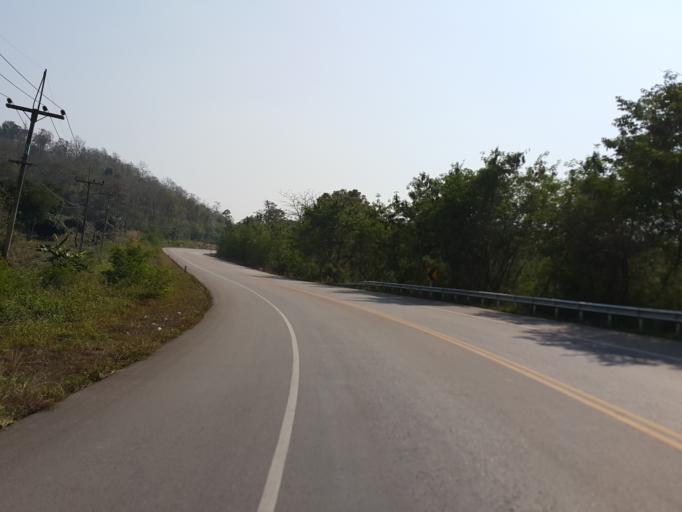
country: TH
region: Lampang
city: Mueang Pan
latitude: 18.8913
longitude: 99.6035
